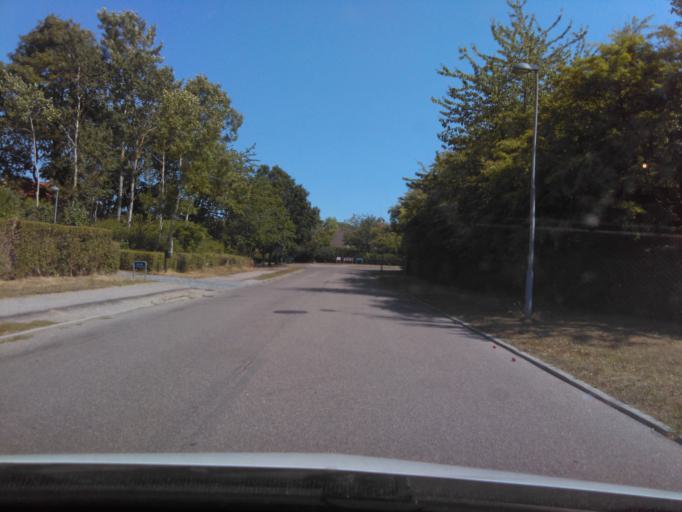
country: DK
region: Capital Region
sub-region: Fureso Kommune
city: Stavnsholt
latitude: 55.8216
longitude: 12.3936
